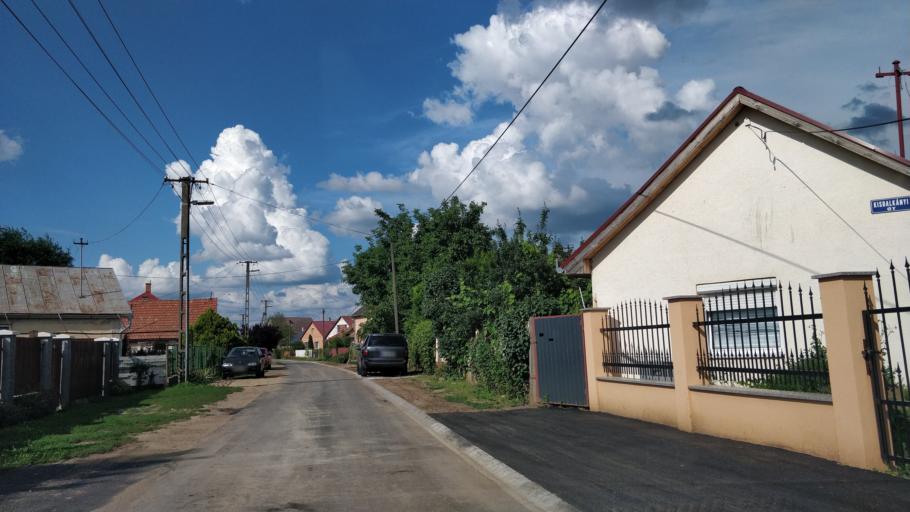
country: HU
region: Szabolcs-Szatmar-Bereg
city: Nagykallo
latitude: 47.8632
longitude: 21.8452
